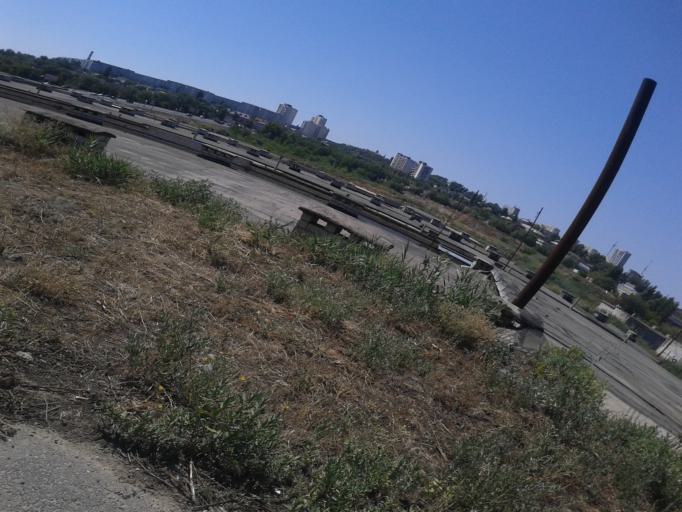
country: RU
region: Volgograd
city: Volgograd
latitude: 48.6884
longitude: 44.4523
